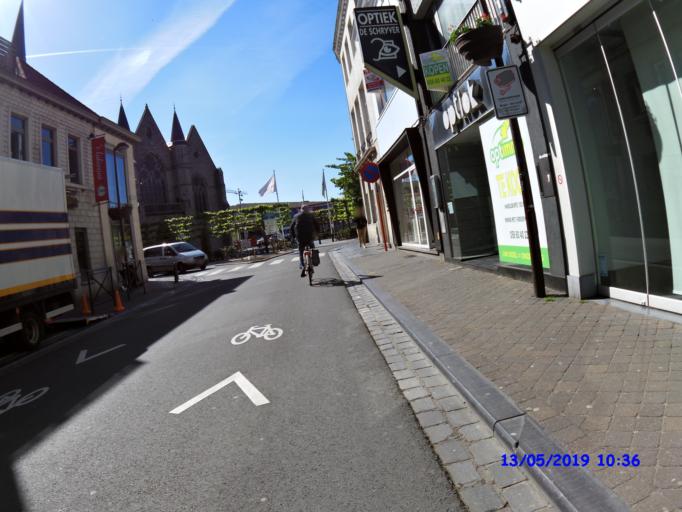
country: BE
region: Flanders
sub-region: Provincie West-Vlaanderen
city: Waregem
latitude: 50.8872
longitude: 3.4315
